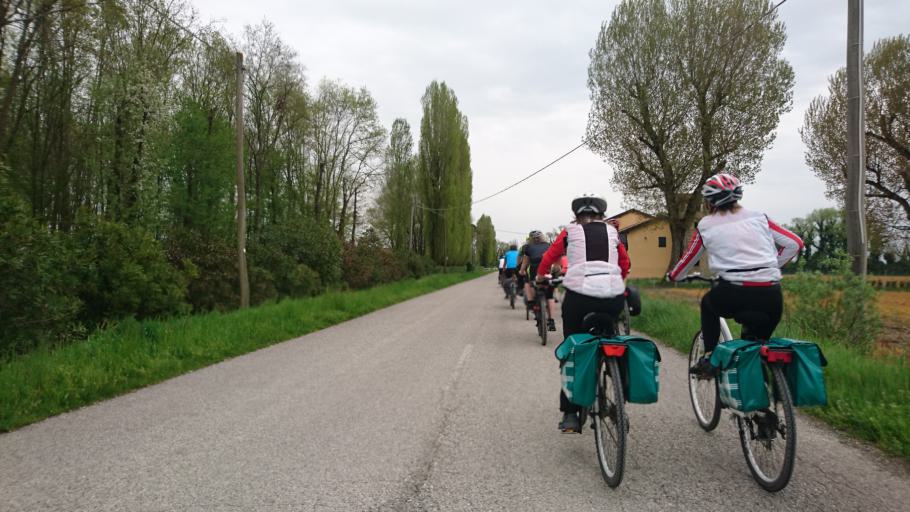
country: IT
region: Veneto
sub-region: Provincia di Venezia
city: Lugugnana
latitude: 45.6992
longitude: 12.8958
